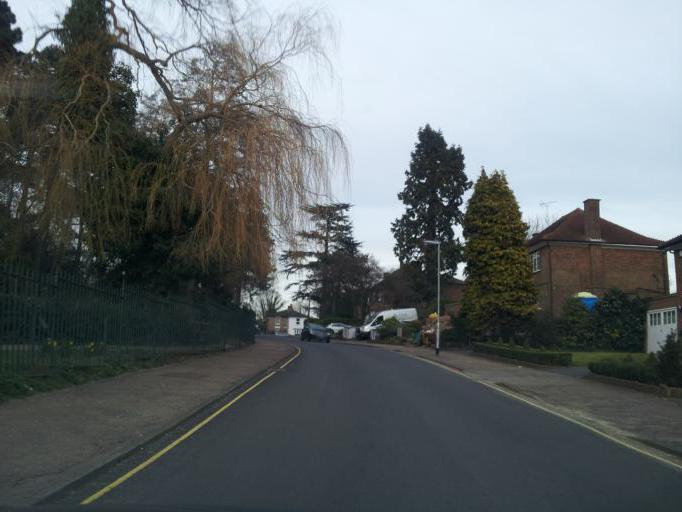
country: GB
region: England
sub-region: Hertfordshire
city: Bushey
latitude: 51.6353
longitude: -0.3459
